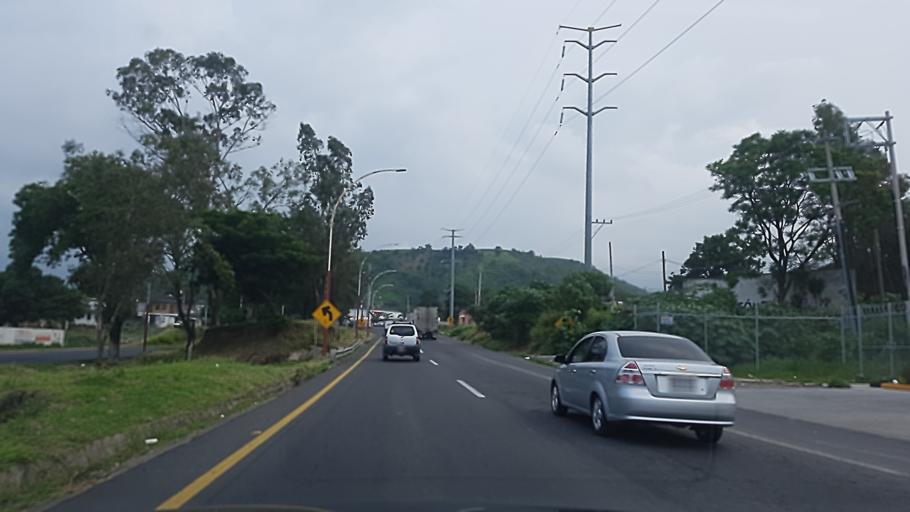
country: MX
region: Nayarit
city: Tepic
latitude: 21.4891
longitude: -104.9038
